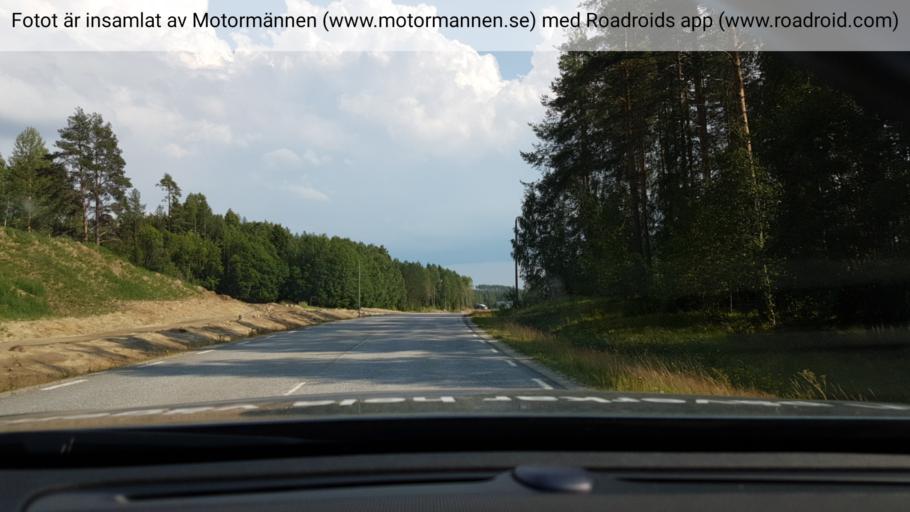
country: SE
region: Vaesterbotten
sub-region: Bjurholms Kommun
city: Bjurholm
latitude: 64.2393
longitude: 19.3370
